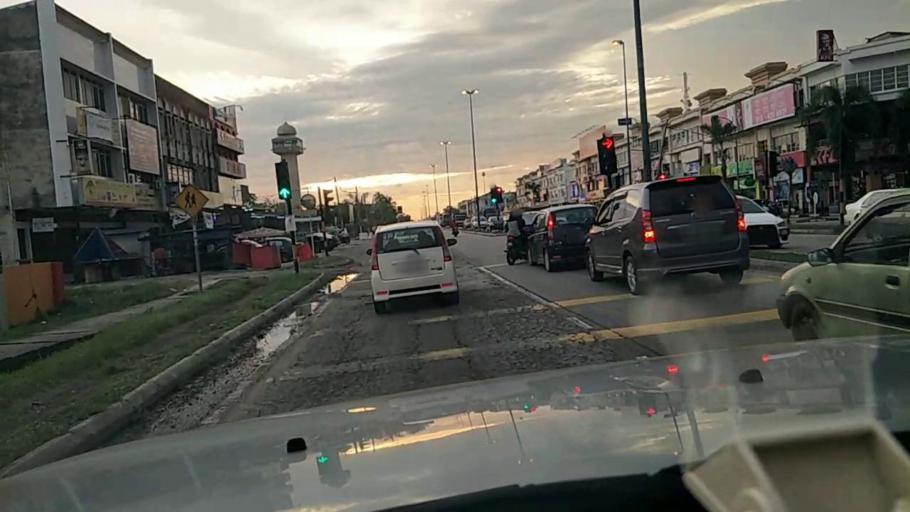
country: MY
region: Perak
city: Kampong Dungun
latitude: 3.1381
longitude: 101.3715
